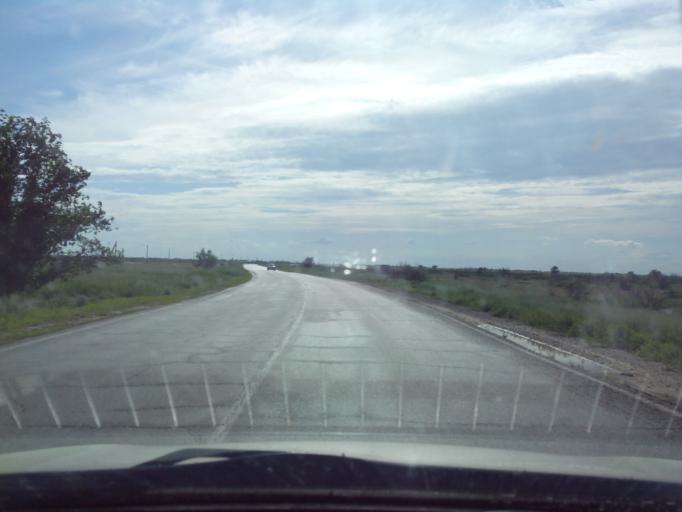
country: RU
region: Astrakhan
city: Znamensk
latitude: 48.5897
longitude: 45.6886
